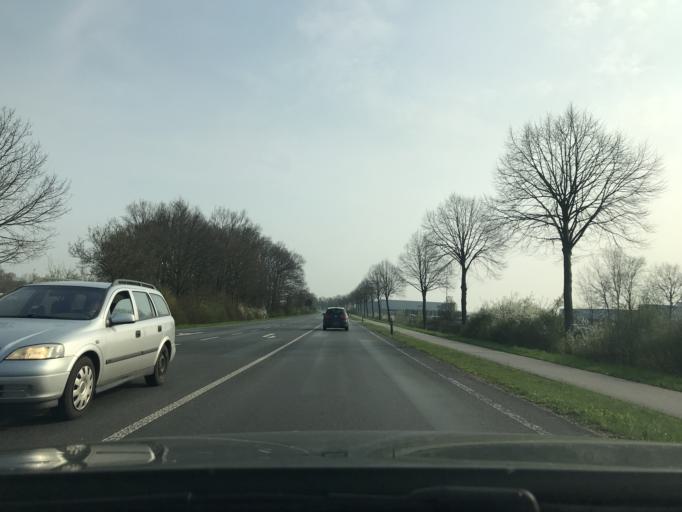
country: DE
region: North Rhine-Westphalia
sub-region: Regierungsbezirk Dusseldorf
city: Kevelaer
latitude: 51.5672
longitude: 6.2641
